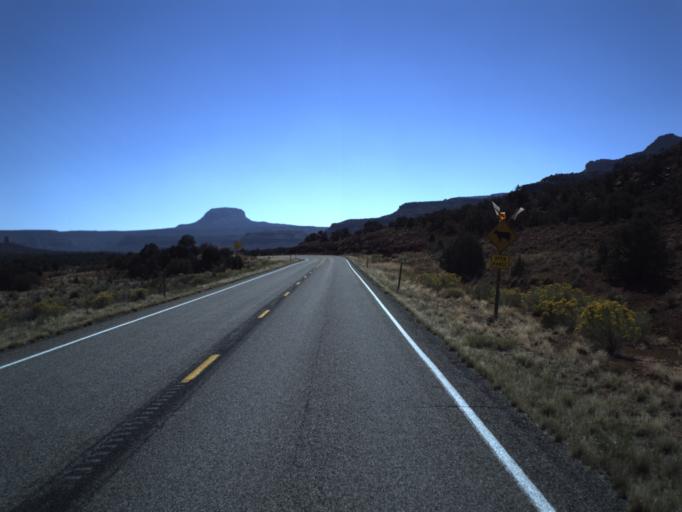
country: US
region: Utah
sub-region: San Juan County
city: Blanding
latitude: 37.6392
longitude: -110.1612
